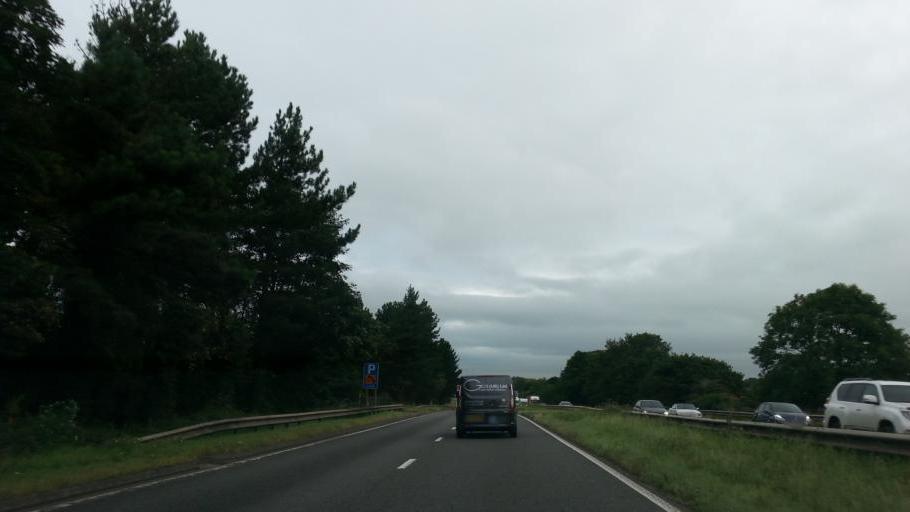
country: GB
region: England
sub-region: Nottinghamshire
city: Babworth
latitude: 53.3197
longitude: -1.0280
